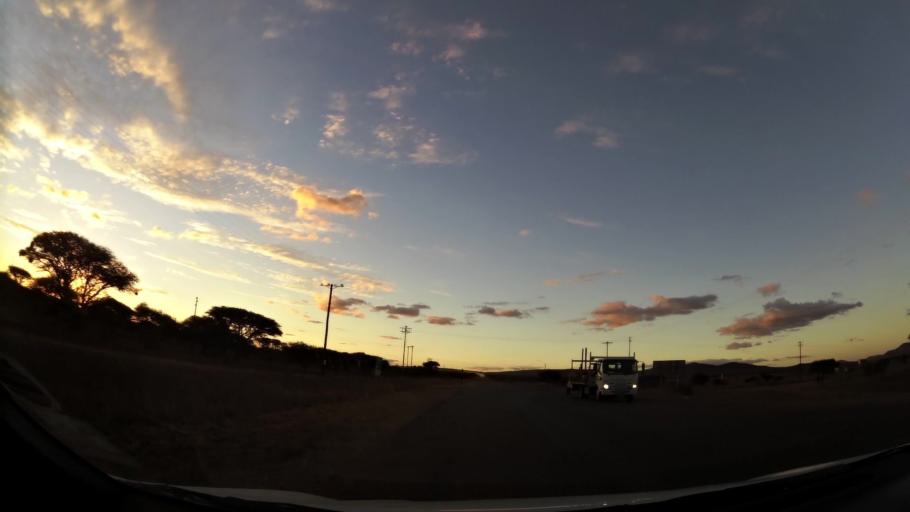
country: ZA
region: Limpopo
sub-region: Capricorn District Municipality
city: Polokwane
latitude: -23.7405
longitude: 29.4697
